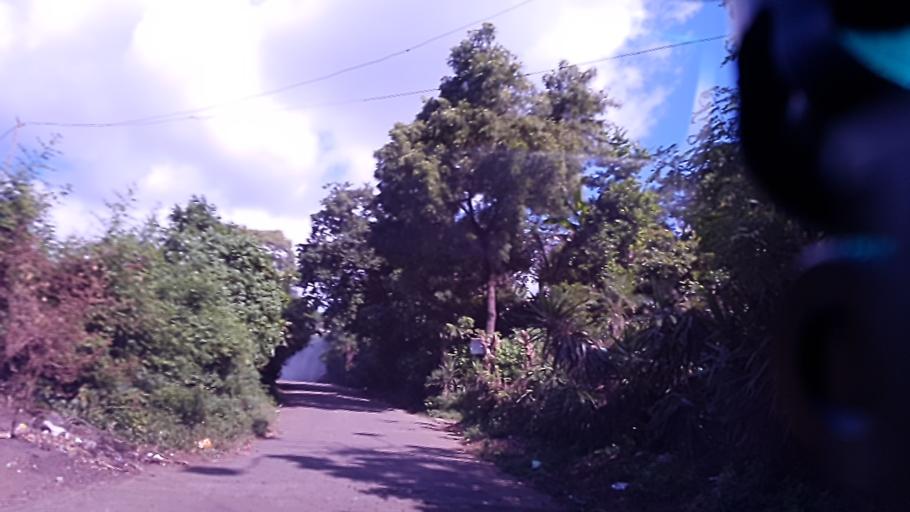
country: NI
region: Masaya
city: Ticuantepe
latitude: 11.9861
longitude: -86.2318
